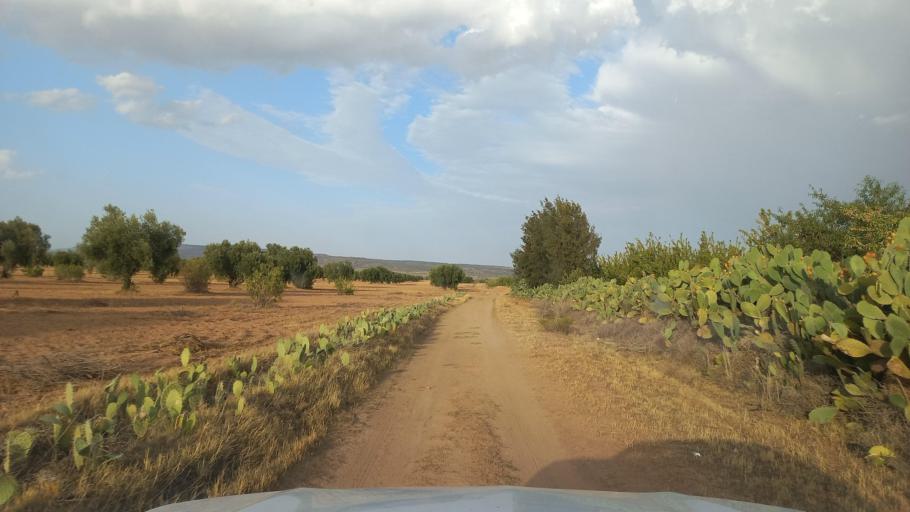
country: TN
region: Al Qasrayn
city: Sbiba
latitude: 35.2867
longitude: 9.0781
